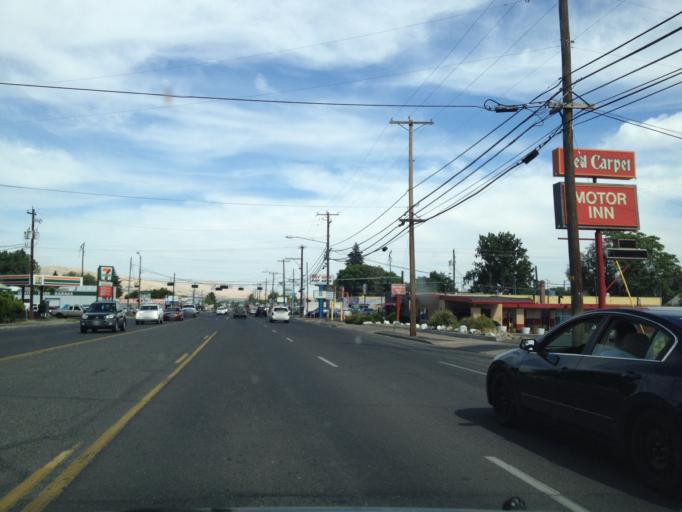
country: US
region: Washington
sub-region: Yakima County
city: Yakima
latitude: 46.6125
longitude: -120.5322
